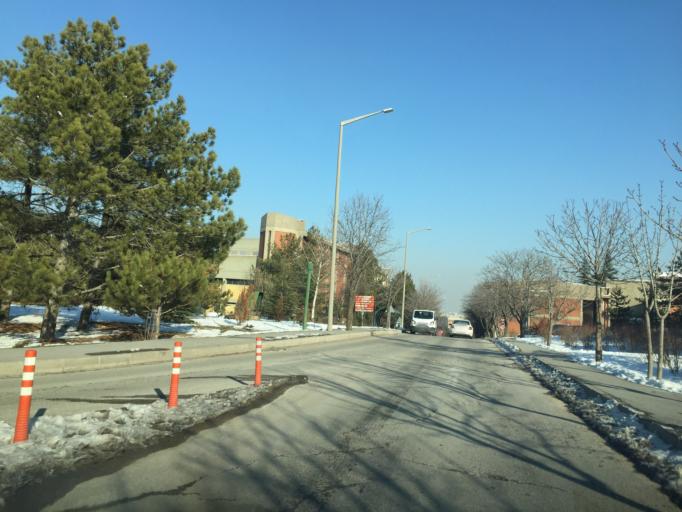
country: TR
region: Ankara
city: Ankara
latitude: 39.8870
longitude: 32.7818
